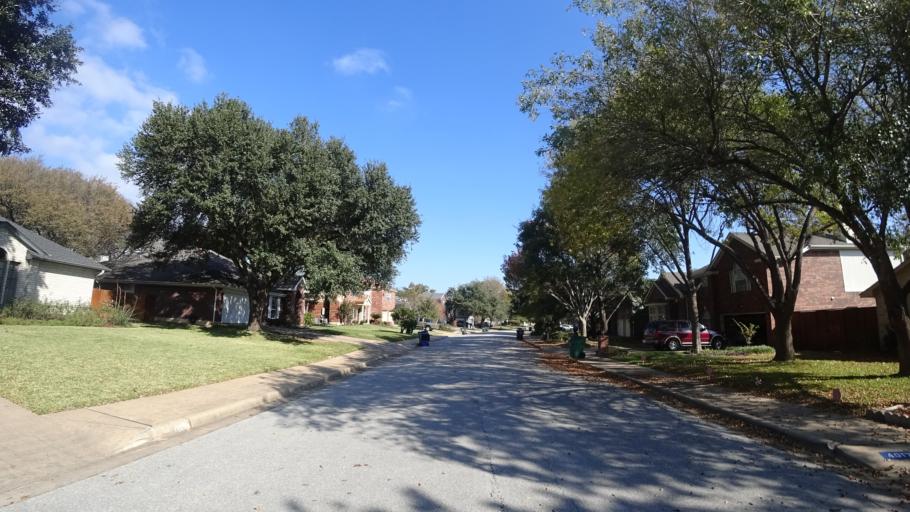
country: US
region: Texas
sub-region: Travis County
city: Shady Hollow
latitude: 30.1697
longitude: -97.8681
